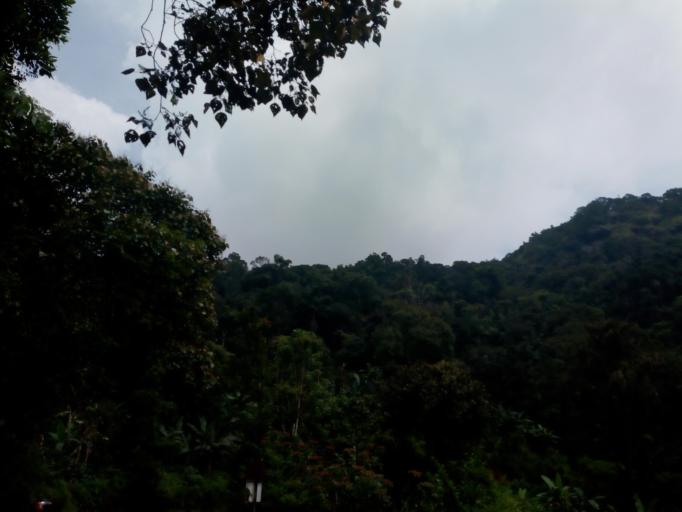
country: IN
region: Karnataka
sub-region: Dakshina Kannada
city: Sulya
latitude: 12.3814
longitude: 75.5118
